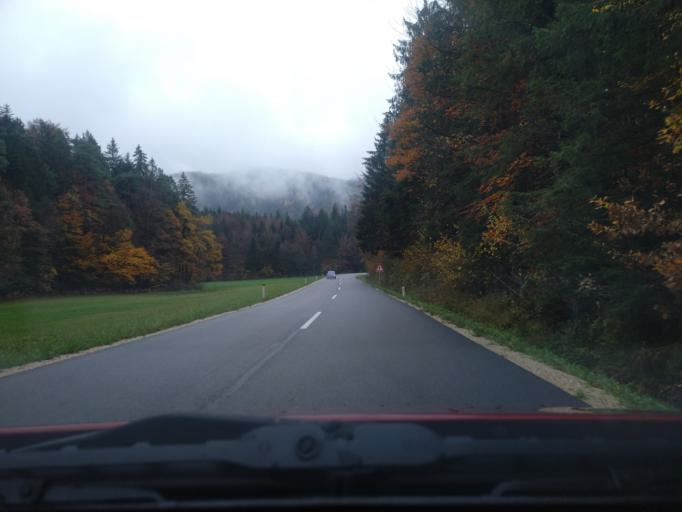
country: SI
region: Ljubno
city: Ljubno ob Savinji
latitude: 46.3214
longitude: 14.8492
